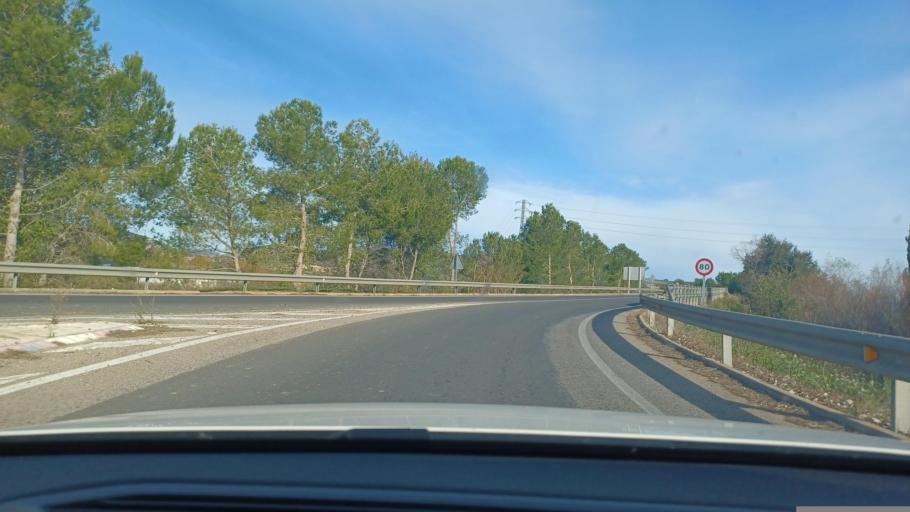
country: ES
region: Catalonia
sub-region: Provincia de Tarragona
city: Ulldecona
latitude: 40.5990
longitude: 0.4548
